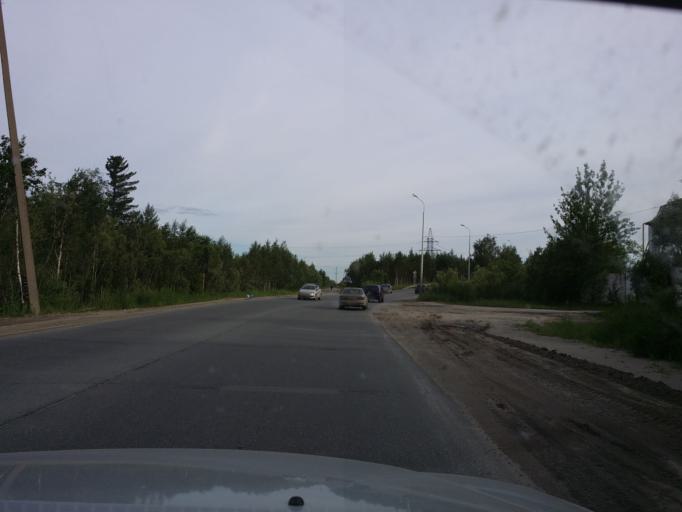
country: RU
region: Khanty-Mansiyskiy Avtonomnyy Okrug
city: Nizhnevartovsk
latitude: 60.9563
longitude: 76.6639
